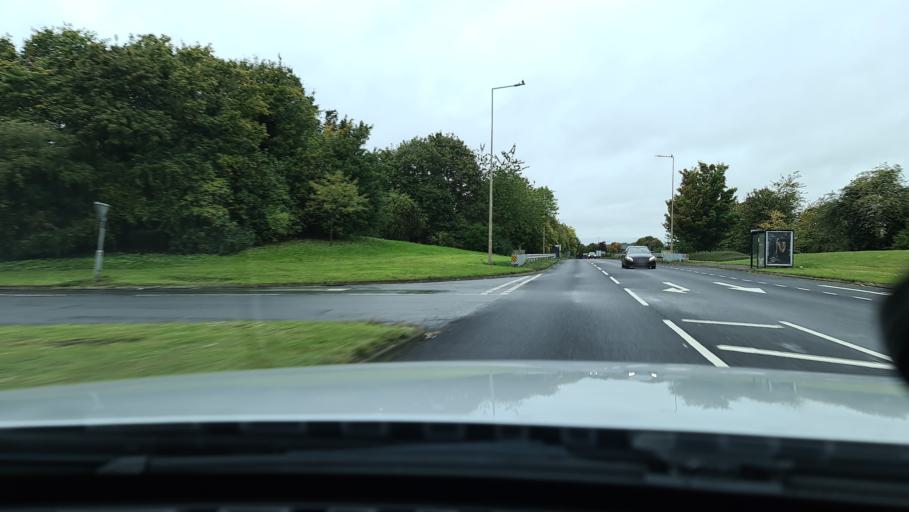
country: GB
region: England
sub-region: Milton Keynes
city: Stony Stratford
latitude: 52.0561
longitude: -0.8225
